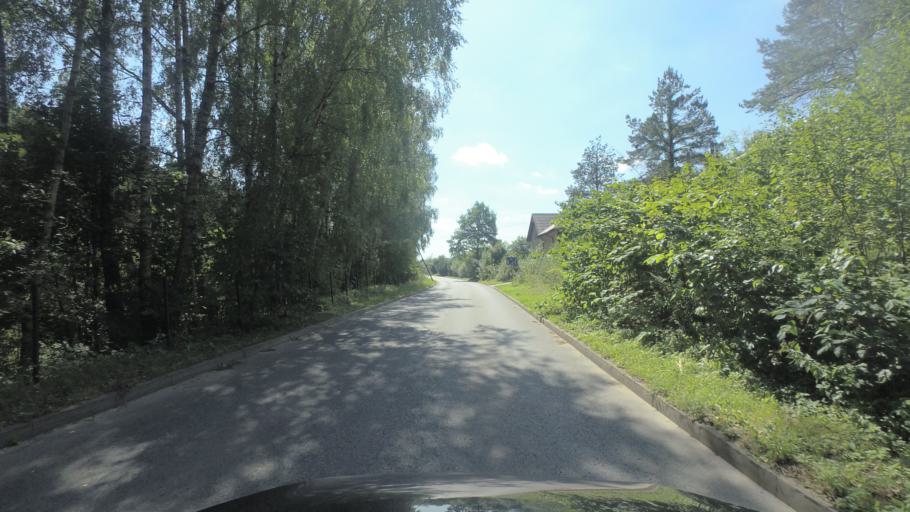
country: LT
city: Nemencine
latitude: 54.8435
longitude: 25.3719
